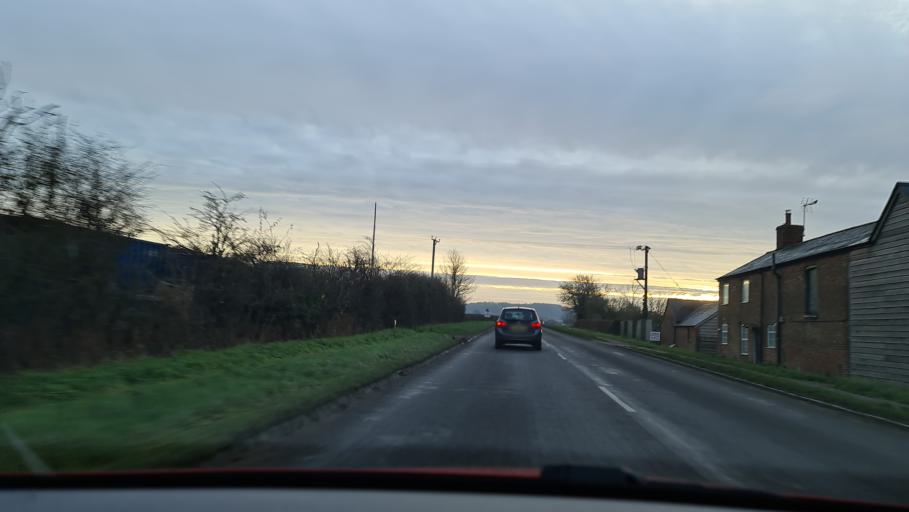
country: GB
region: England
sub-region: Buckinghamshire
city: Princes Risborough
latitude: 51.7482
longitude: -0.8731
